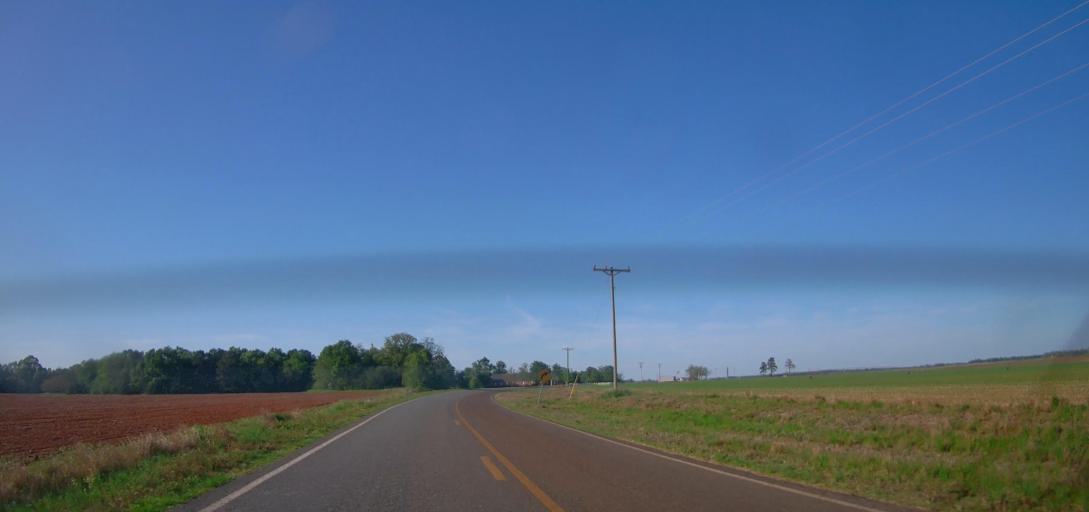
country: US
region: Georgia
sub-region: Macon County
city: Montezuma
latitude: 32.3512
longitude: -83.9437
